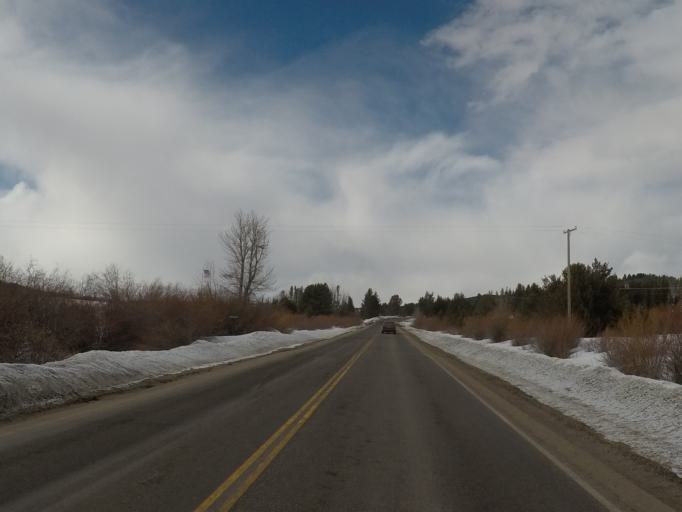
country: US
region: Montana
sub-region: Granite County
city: Philipsburg
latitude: 46.1952
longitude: -113.2669
